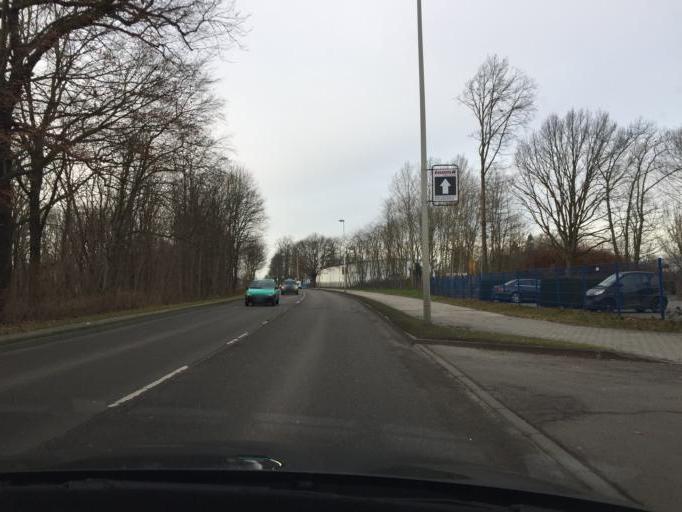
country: DE
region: Brandenburg
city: Cottbus
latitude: 51.7703
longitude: 14.3513
